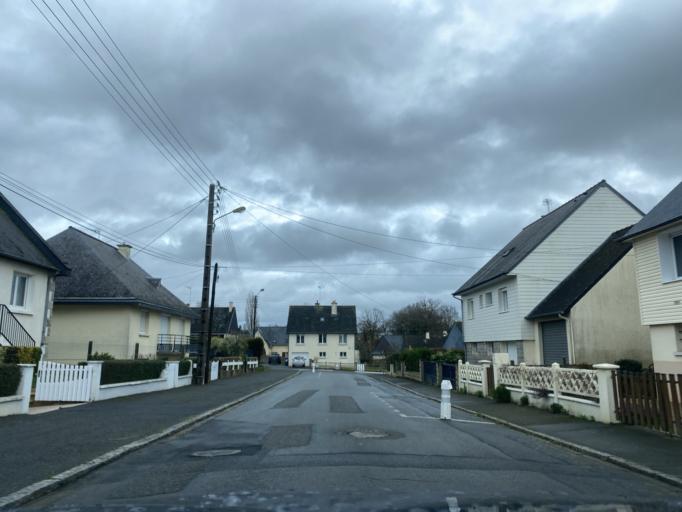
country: FR
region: Brittany
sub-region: Departement d'Ille-et-Vilaine
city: Melesse
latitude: 48.2163
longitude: -1.6934
